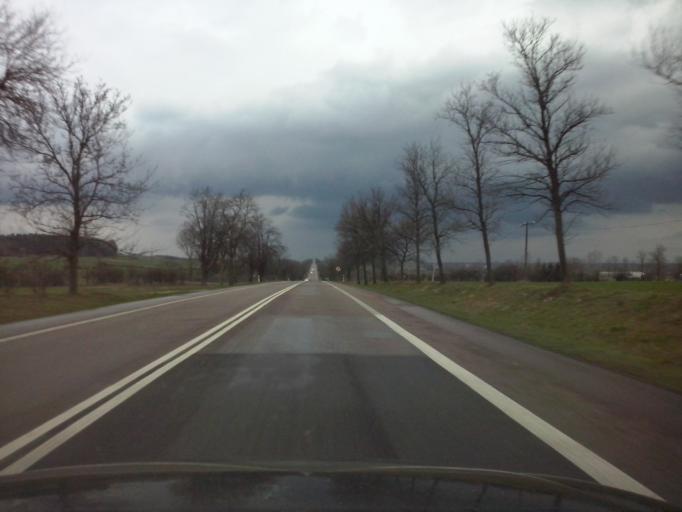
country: PL
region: Lublin Voivodeship
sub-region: Powiat chelmski
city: Rejowiec Fabryczny
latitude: 51.1748
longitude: 23.2589
